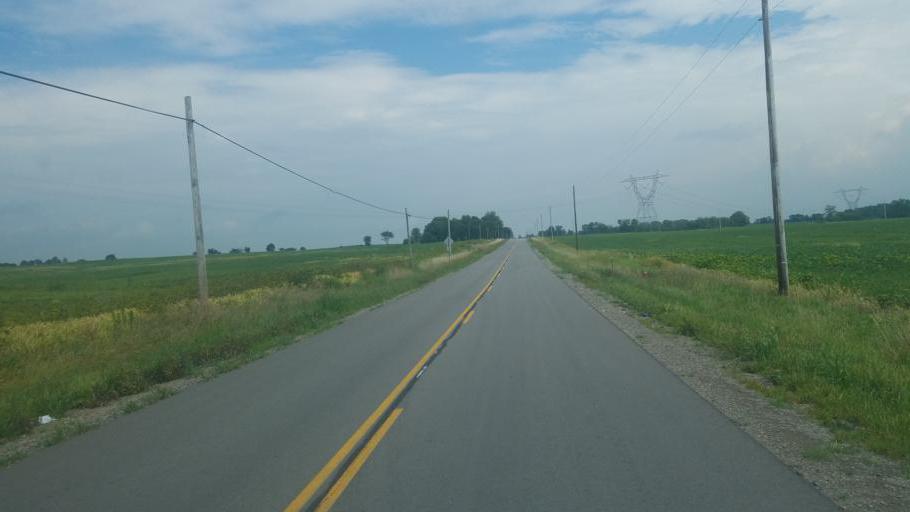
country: US
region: Ohio
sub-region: Logan County
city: Northwood
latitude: 40.3915
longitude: -83.5870
